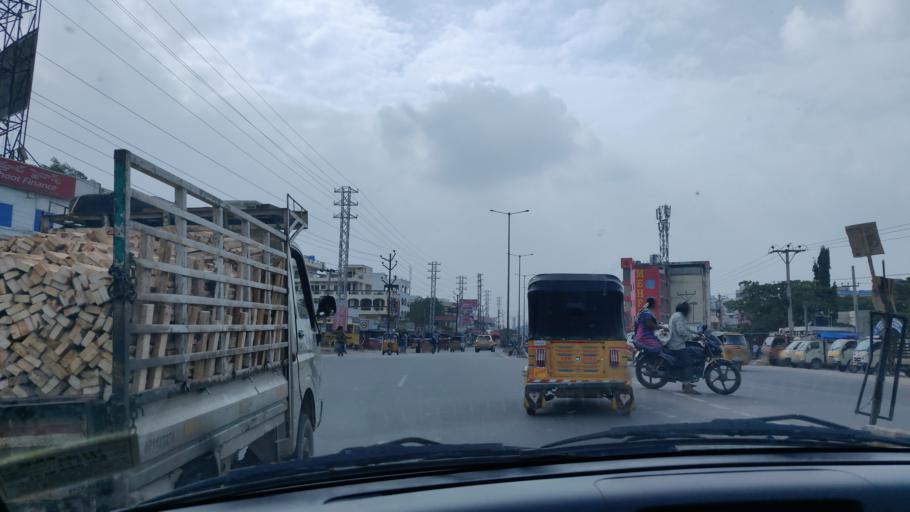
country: IN
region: Telangana
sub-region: Rangareddi
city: Balapur
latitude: 17.3163
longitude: 78.4511
